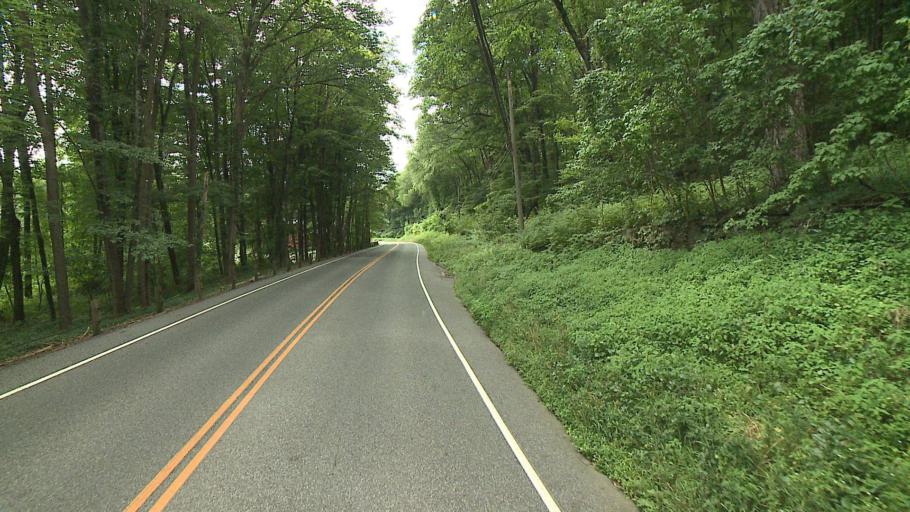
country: US
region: Connecticut
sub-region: Fairfield County
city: Sherman
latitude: 41.6222
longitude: -73.5077
